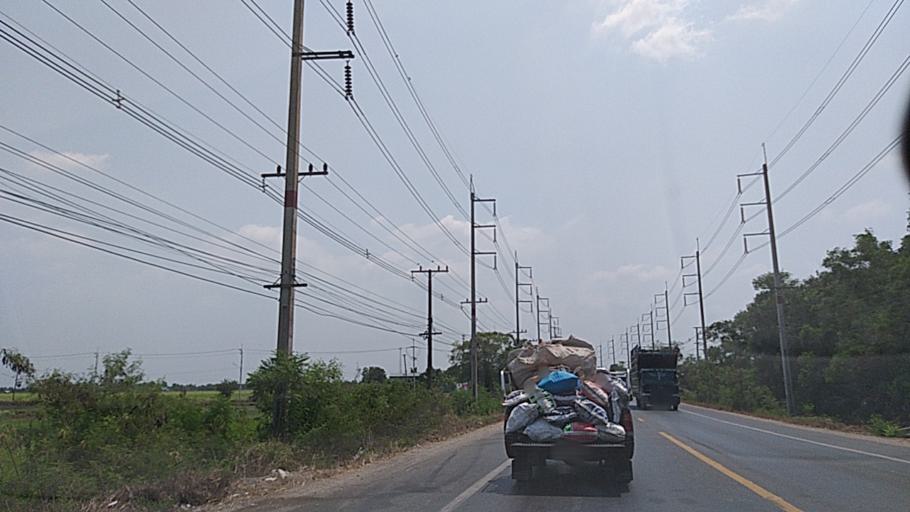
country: TH
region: Chachoengsao
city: Bang Nam Priao
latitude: 13.7785
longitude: 101.0626
